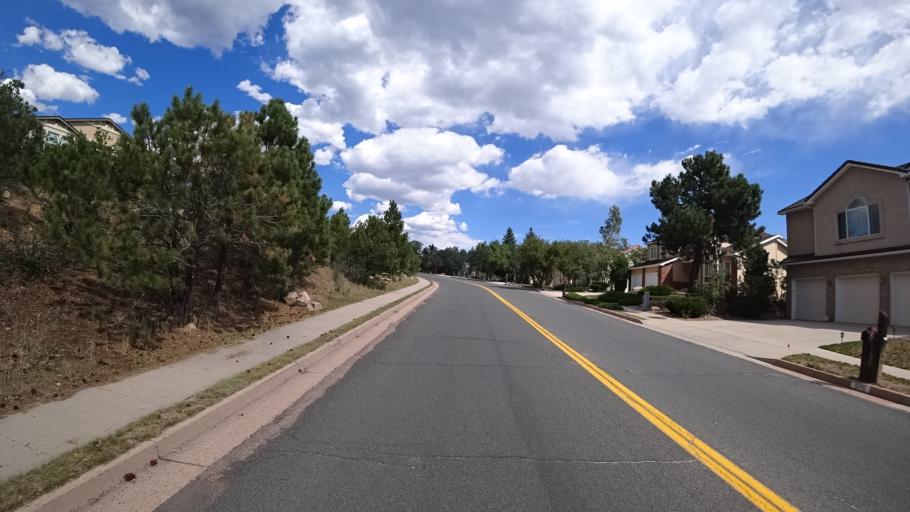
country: US
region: Colorado
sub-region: El Paso County
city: Fort Carson
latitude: 38.7603
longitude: -104.8273
